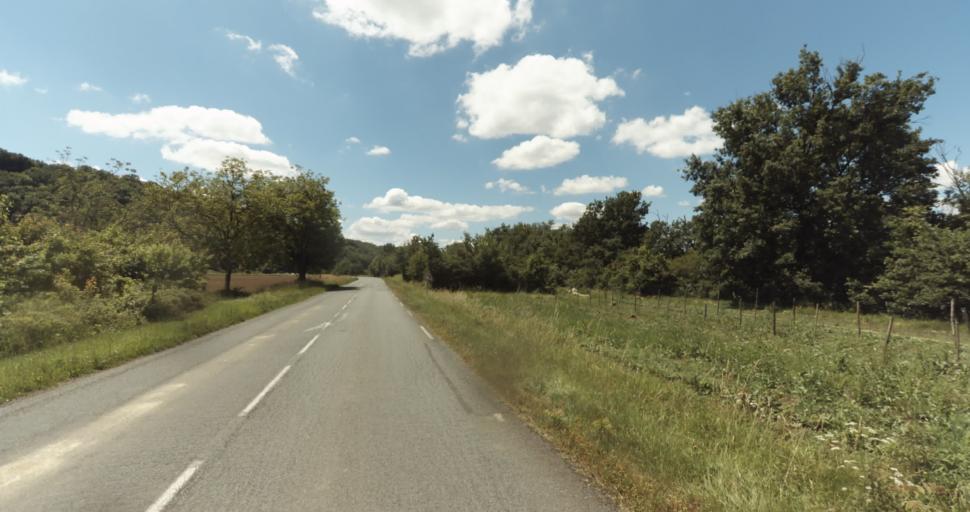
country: FR
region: Aquitaine
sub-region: Departement de la Dordogne
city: Lalinde
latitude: 44.8362
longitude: 0.7540
